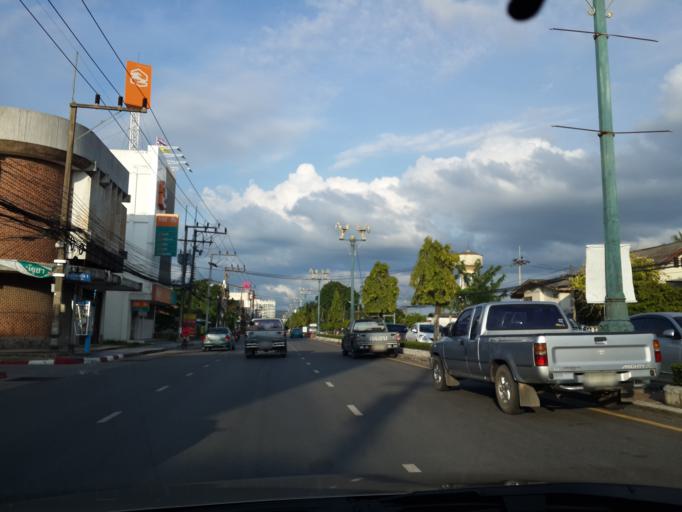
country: TH
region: Yala
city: Yala
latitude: 6.5494
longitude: 101.2779
